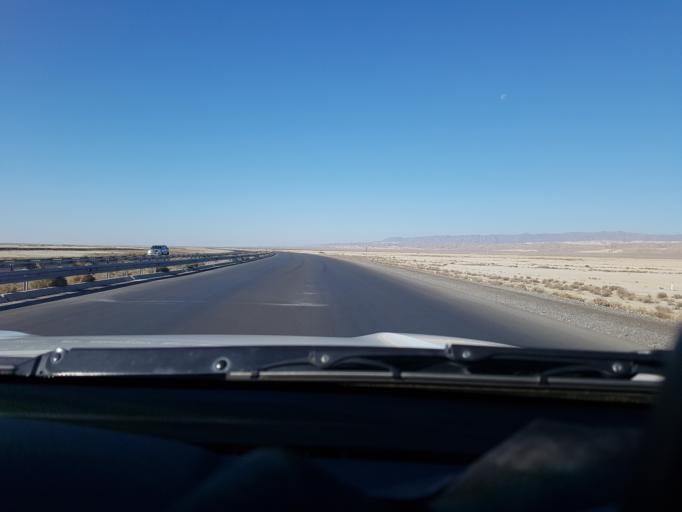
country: TM
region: Balkan
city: Gazanjyk
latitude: 39.2711
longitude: 55.1479
